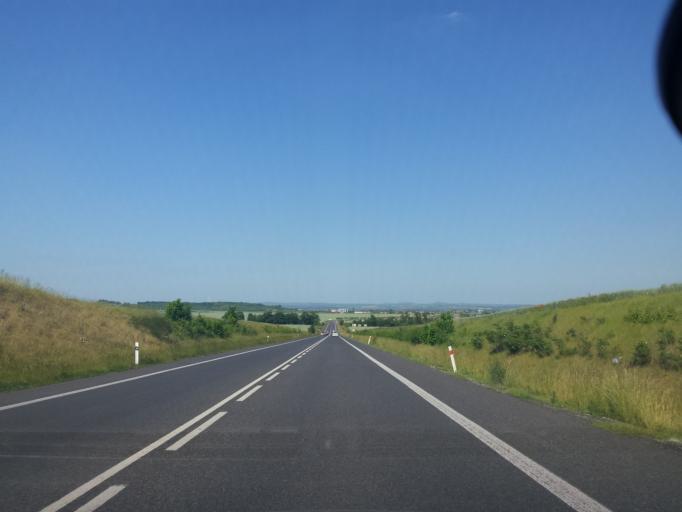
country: CZ
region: Central Bohemia
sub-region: Okres Melnik
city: Veltrusy
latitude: 50.3162
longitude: 14.3293
